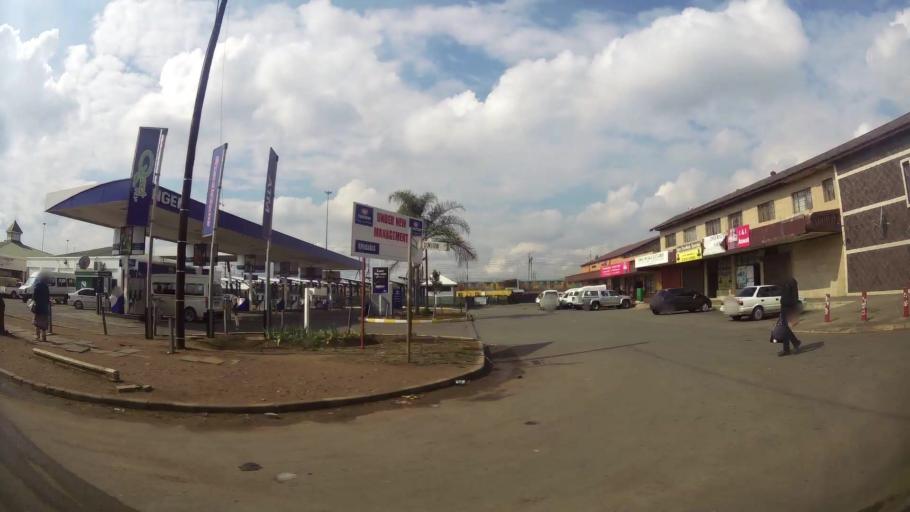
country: ZA
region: Gauteng
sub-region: Sedibeng District Municipality
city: Vereeniging
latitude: -26.6794
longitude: 27.9329
